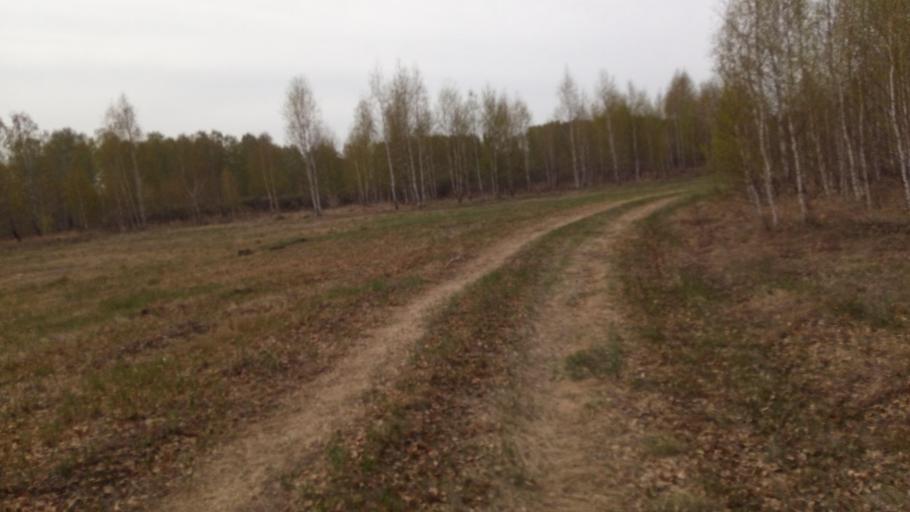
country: RU
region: Chelyabinsk
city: Timiryazevskiy
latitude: 55.0075
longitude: 60.8586
